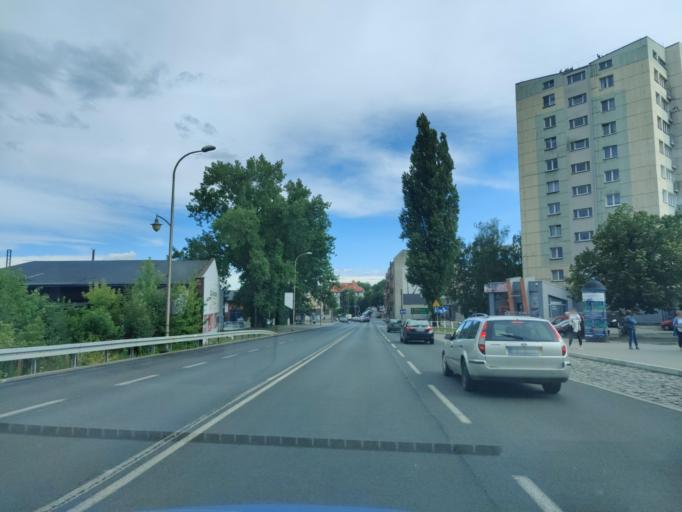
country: PL
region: Silesian Voivodeship
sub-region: Myslowice
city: Myslowice
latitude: 50.2431
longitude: 19.1342
